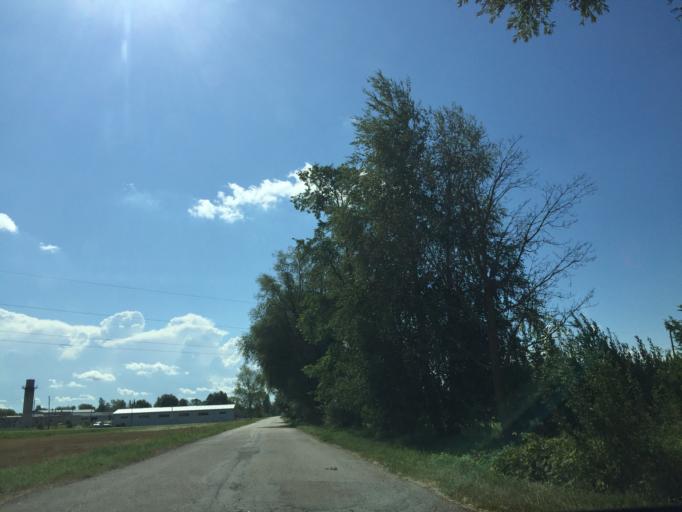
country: LV
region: Bauskas Rajons
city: Bauska
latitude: 56.4190
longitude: 24.1752
